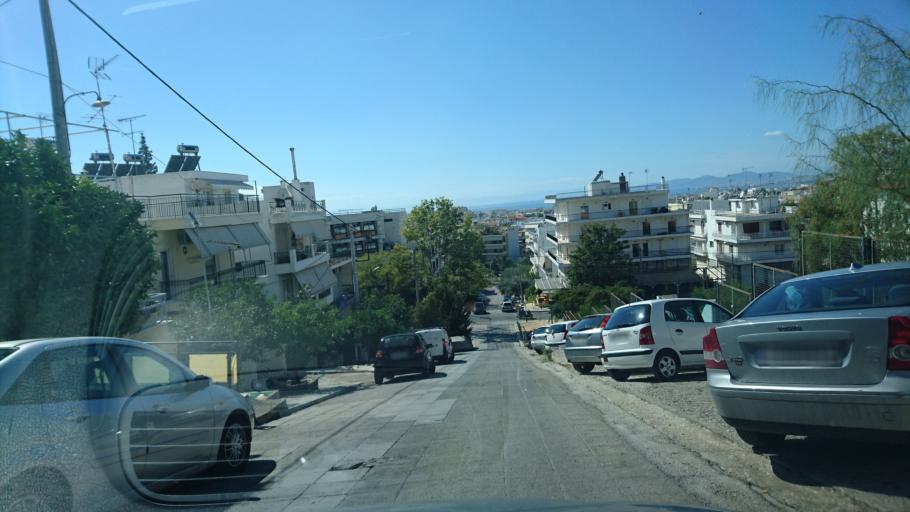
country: GR
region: Attica
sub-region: Nomarchia Athinas
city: Ilioupoli
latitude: 37.9360
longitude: 23.7536
